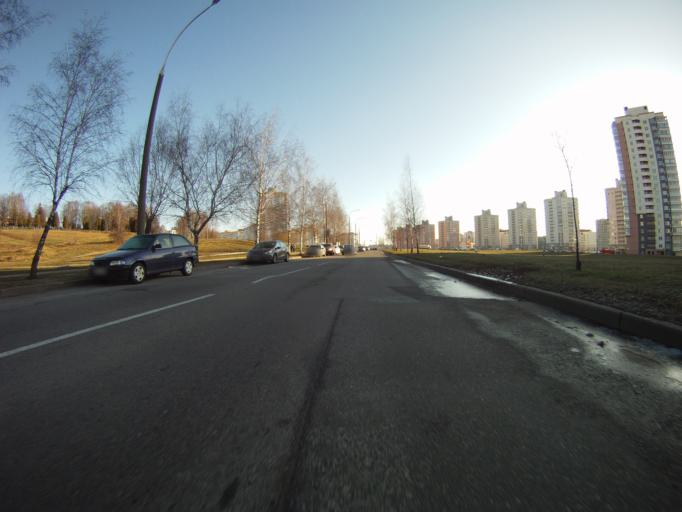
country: BY
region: Minsk
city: Novoye Medvezhino
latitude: 53.8791
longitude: 27.4461
